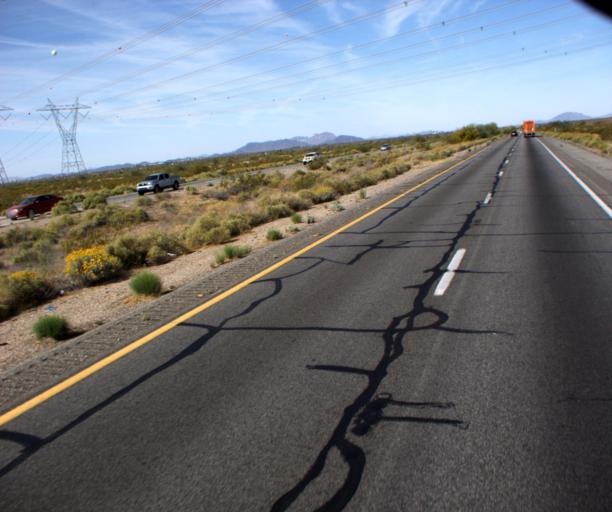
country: US
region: Arizona
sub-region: Maricopa County
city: Buckeye
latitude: 33.4528
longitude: -112.7371
